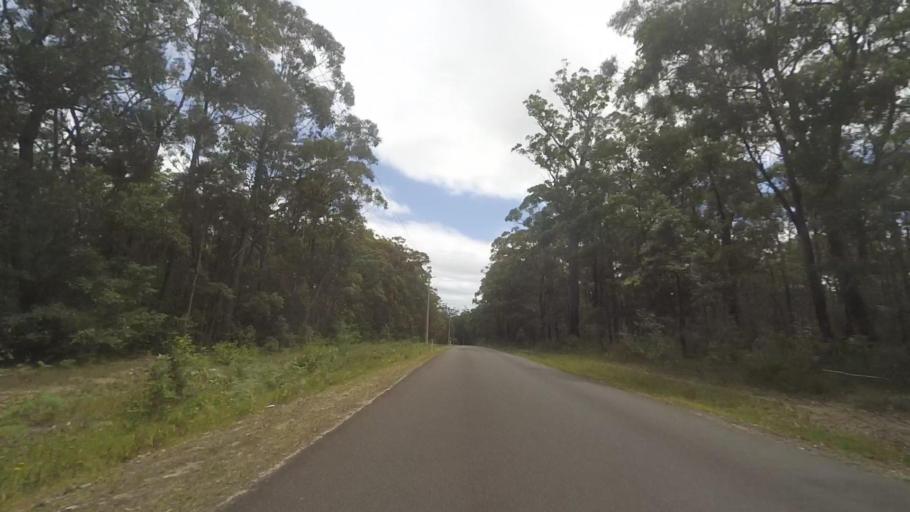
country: AU
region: New South Wales
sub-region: Shoalhaven Shire
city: Milton
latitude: -35.3827
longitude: 150.3694
